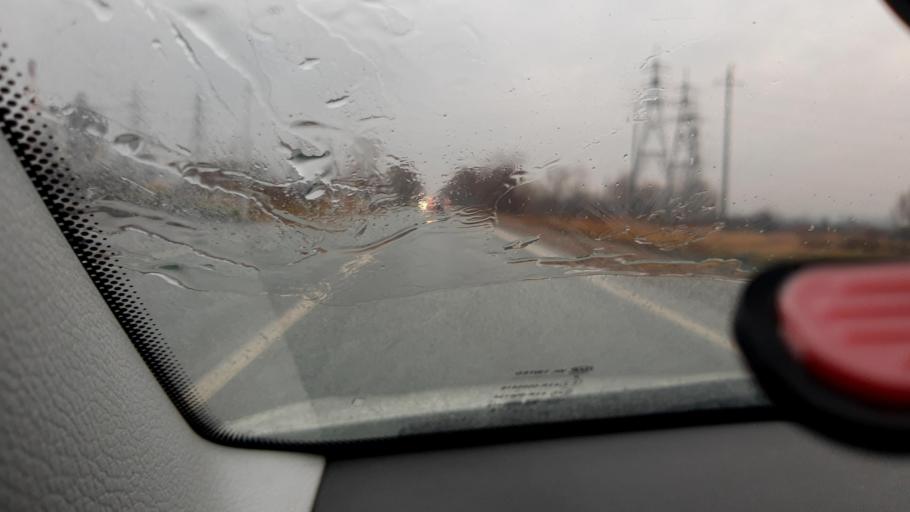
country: RU
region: Bashkortostan
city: Ufa
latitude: 54.8472
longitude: 56.1193
